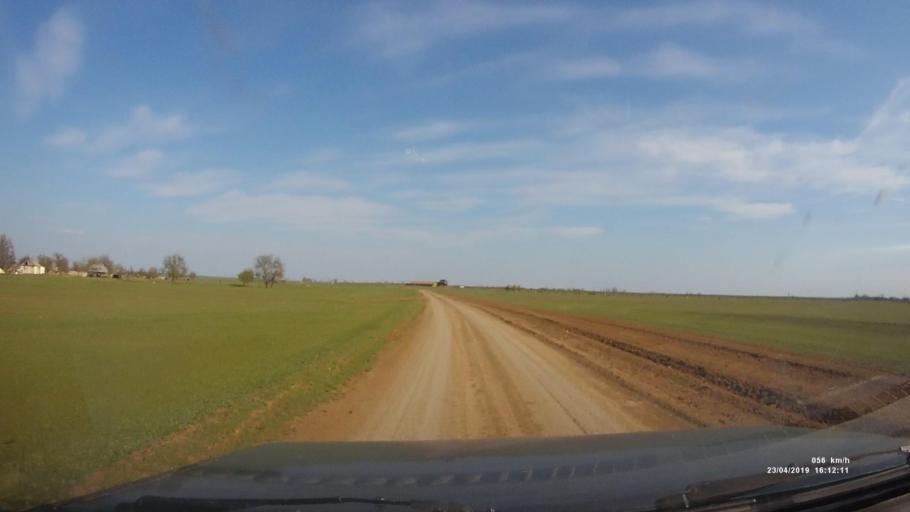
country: RU
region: Kalmykiya
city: Priyutnoye
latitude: 46.4678
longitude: 43.1240
